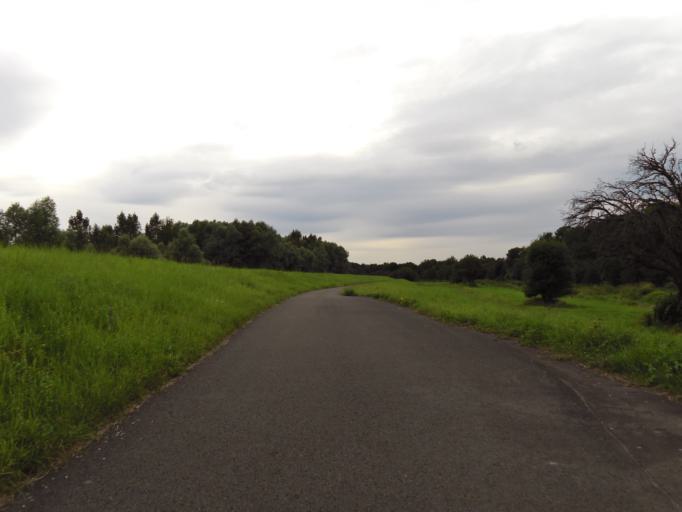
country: DE
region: Rheinland-Pfalz
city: Worms
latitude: 49.6124
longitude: 8.3819
